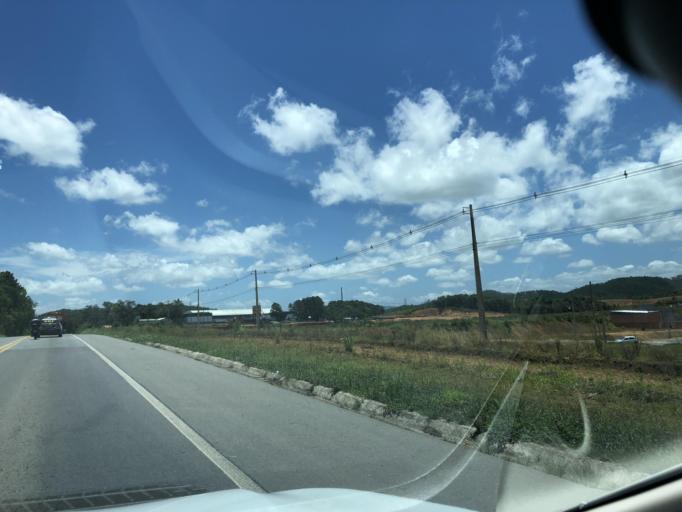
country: BR
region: Santa Catarina
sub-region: Joinville
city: Joinville
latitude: -26.4269
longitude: -48.7896
